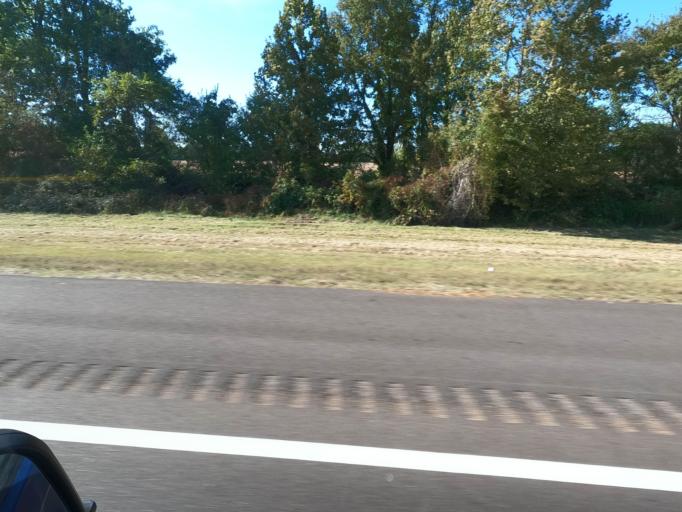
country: US
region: Tennessee
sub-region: Obion County
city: Obion
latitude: 36.2742
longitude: -89.2124
